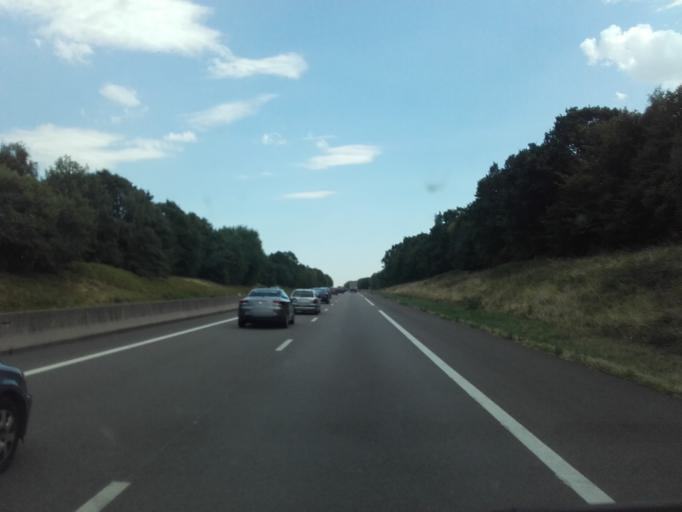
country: FR
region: Bourgogne
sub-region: Departement de la Cote-d'Or
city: Semur-en-Auxois
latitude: 47.4600
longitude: 4.2550
